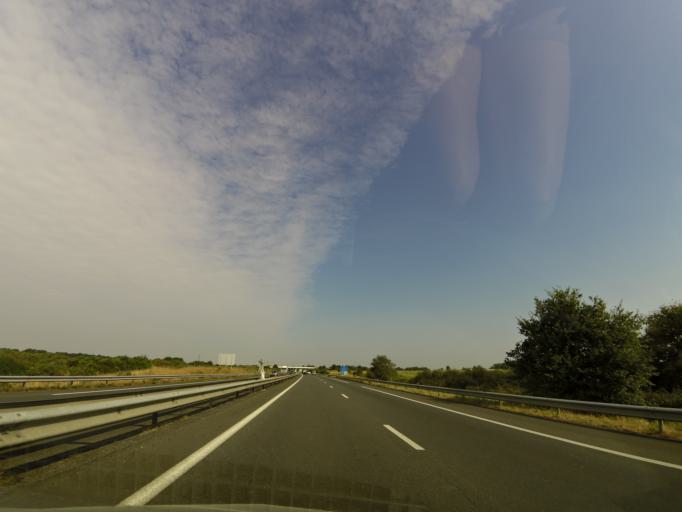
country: FR
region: Pays de la Loire
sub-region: Departement de la Loire-Atlantique
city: La Planche
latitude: 47.0070
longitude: -1.3866
